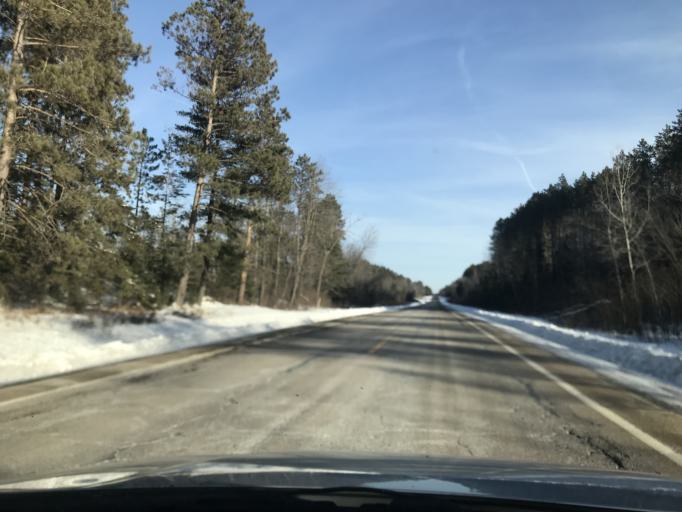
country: US
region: Wisconsin
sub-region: Menominee County
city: Legend Lake
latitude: 45.2016
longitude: -88.5655
